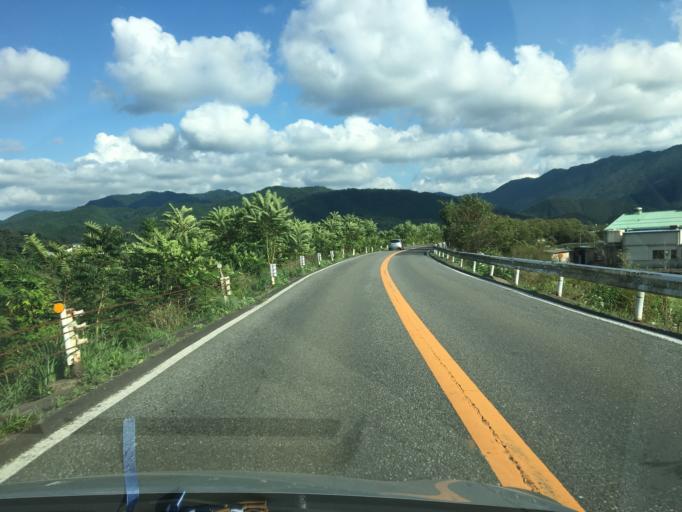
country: JP
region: Hyogo
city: Toyooka
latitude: 35.4399
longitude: 134.7864
